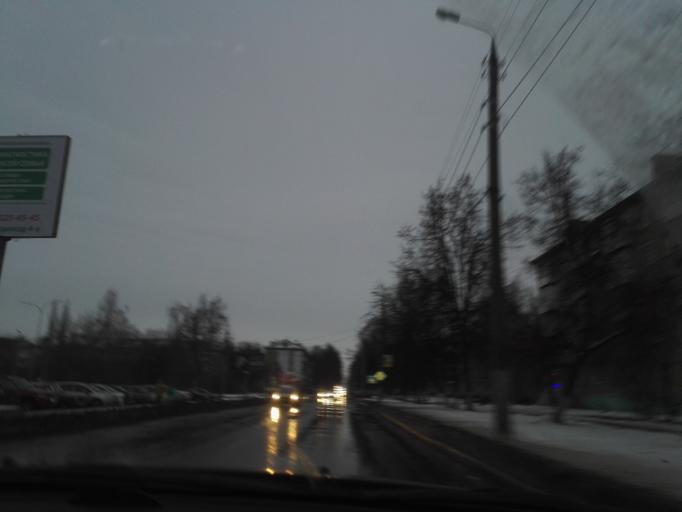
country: RU
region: Tula
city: Novomoskovsk
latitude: 54.0119
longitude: 38.3044
